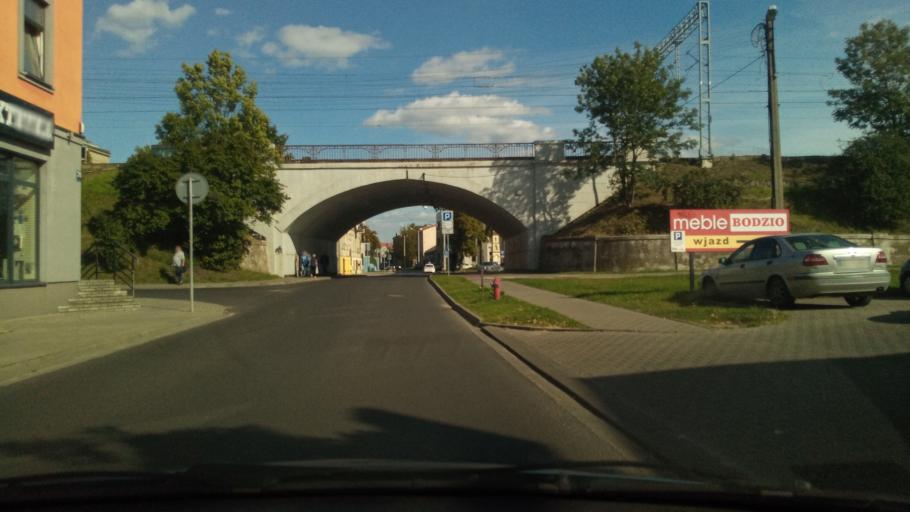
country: PL
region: Lodz Voivodeship
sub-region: Piotrkow Trybunalski
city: Piotrkow Trybunalski
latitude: 51.4074
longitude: 19.6834
